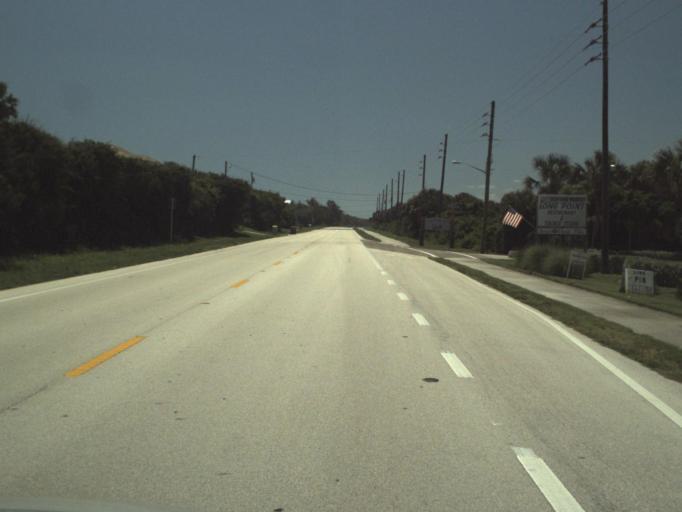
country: US
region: Florida
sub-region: Brevard County
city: Micco
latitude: 27.8836
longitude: -80.4607
